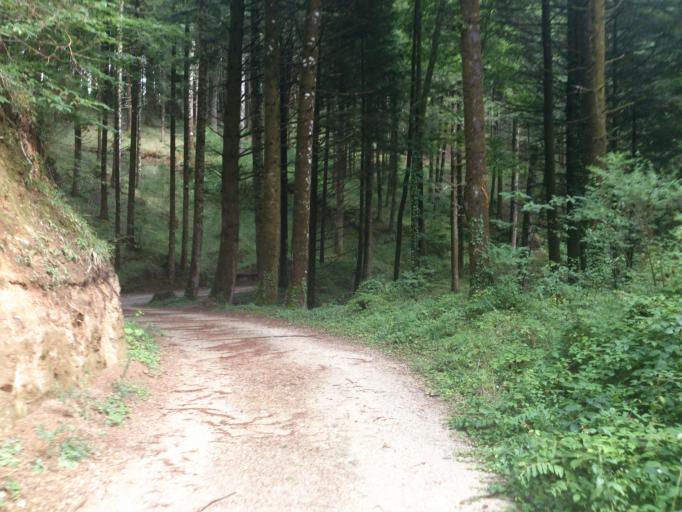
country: IT
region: Calabria
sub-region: Provincia di Vibo-Valentia
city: Serra San Bruno
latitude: 38.5511
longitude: 16.3103
